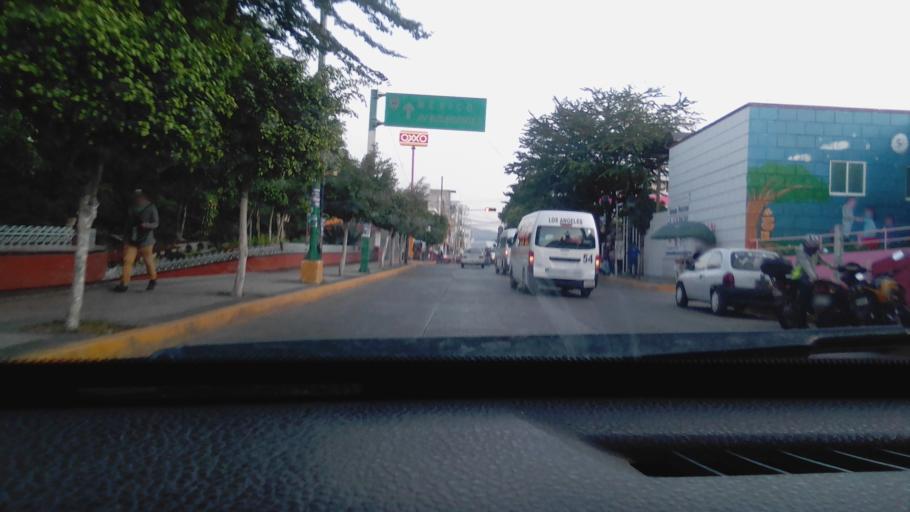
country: MX
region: Guerrero
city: Chilpancingo de los Bravos
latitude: 17.5564
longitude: -99.5039
